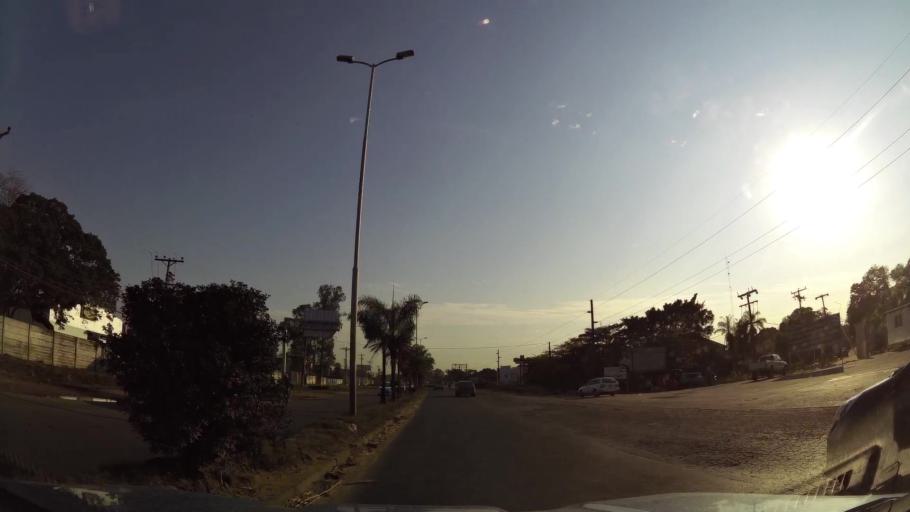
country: BO
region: Santa Cruz
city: Santa Cruz de la Sierra
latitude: -17.7123
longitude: -63.1606
